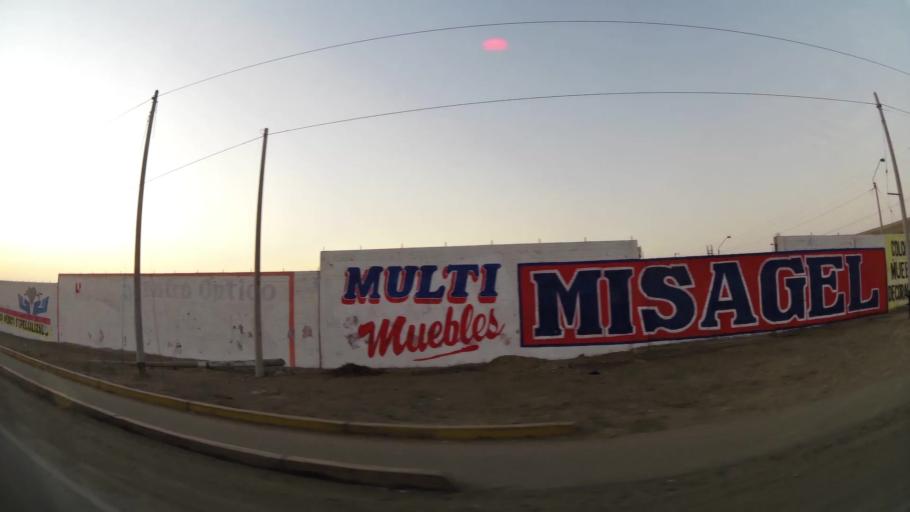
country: PE
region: Ica
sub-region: Provincia de Pisco
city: Pisco
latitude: -13.7108
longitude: -76.1853
